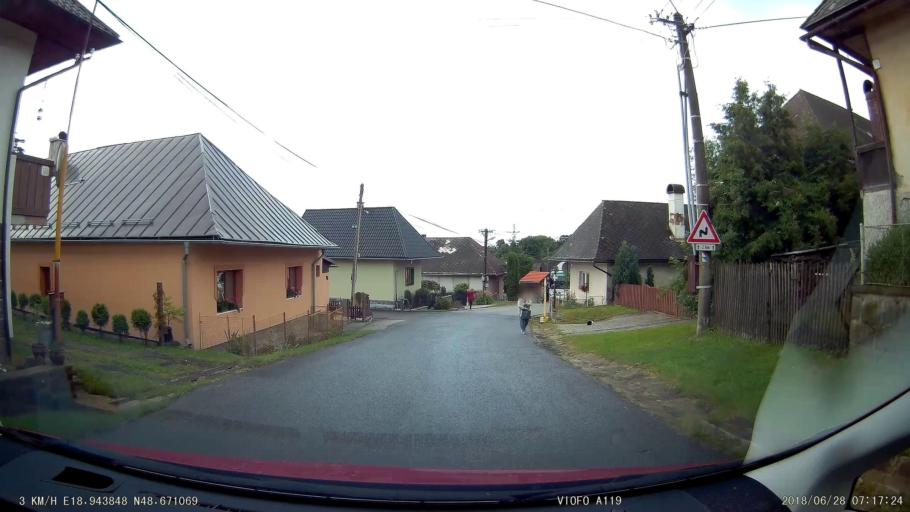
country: SK
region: Banskobystricky
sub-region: Okres Ziar nad Hronom
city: Kremnica
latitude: 48.6711
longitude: 18.9439
